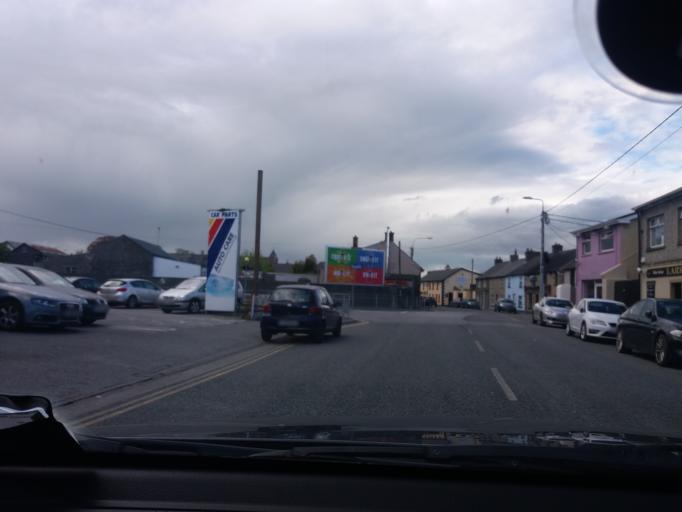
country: IE
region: Leinster
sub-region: Kilkenny
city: Kilkenny
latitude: 52.6453
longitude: -7.2500
